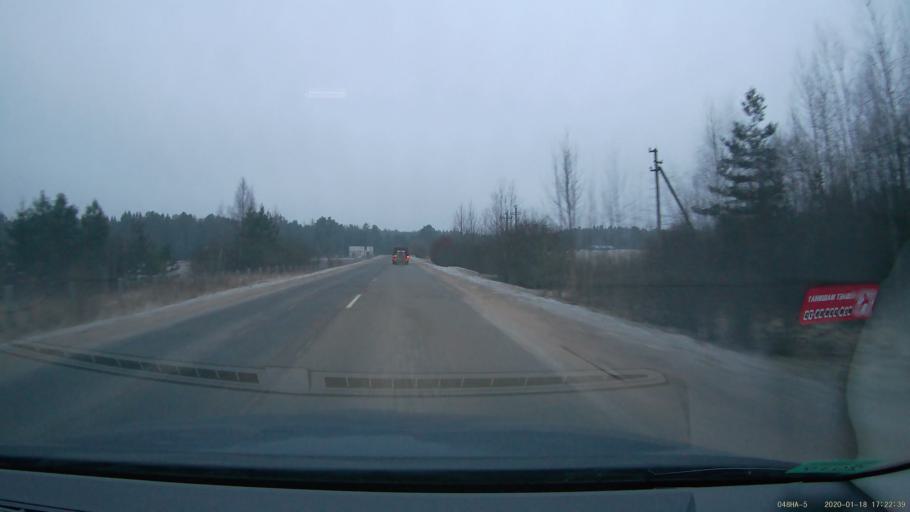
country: BY
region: Minsk
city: Rakaw
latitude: 53.9641
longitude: 27.1210
